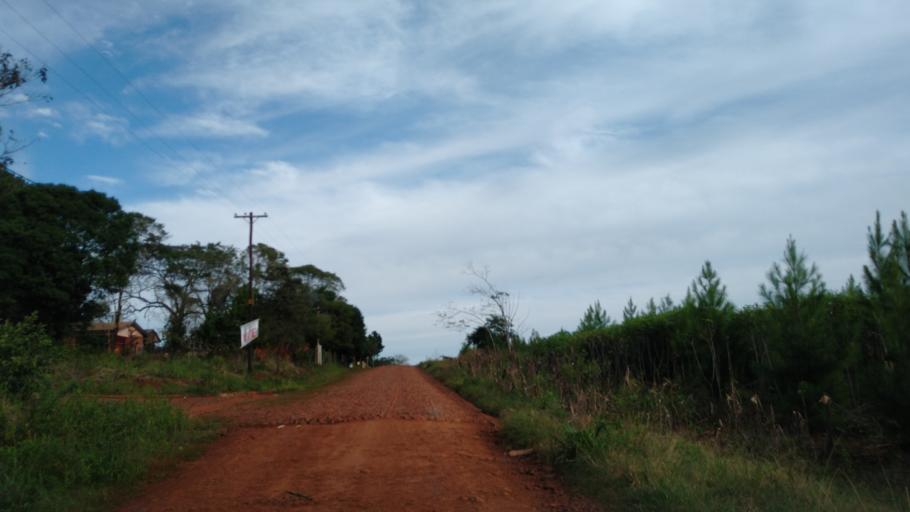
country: AR
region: Misiones
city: Capiovi
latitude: -26.9431
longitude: -55.0965
